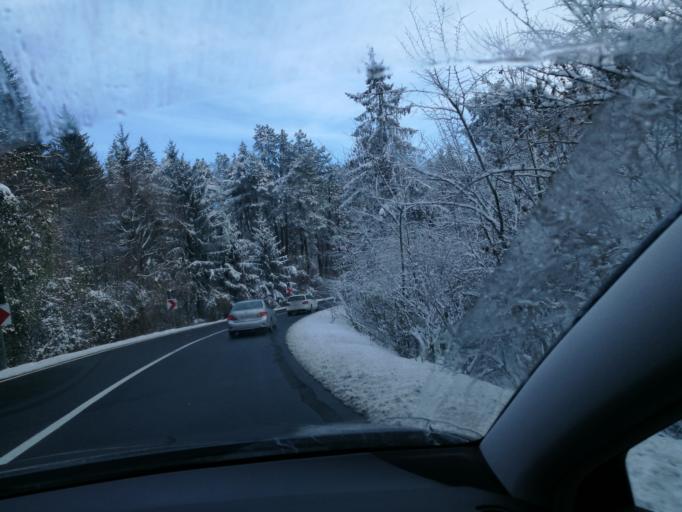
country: RO
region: Brasov
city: Brasov
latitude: 45.6290
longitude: 25.5507
